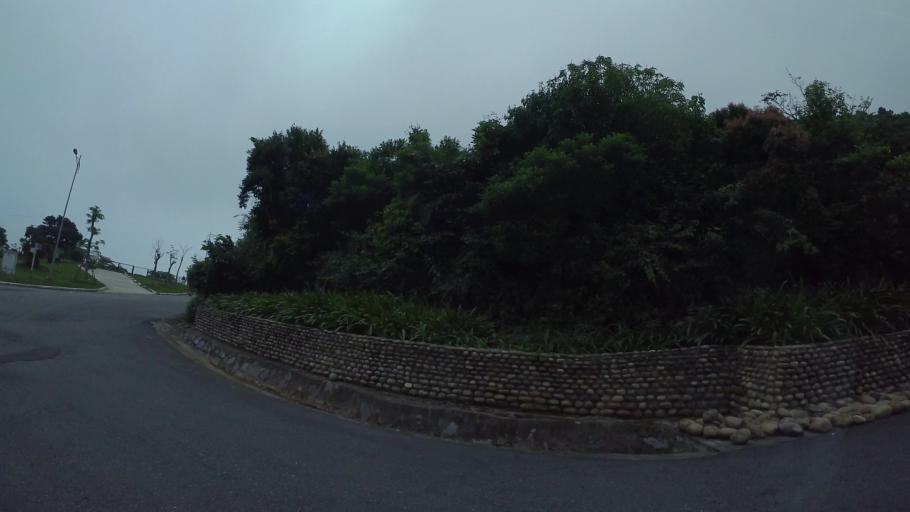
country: VN
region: Da Nang
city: Son Tra
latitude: 16.1168
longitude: 108.3107
